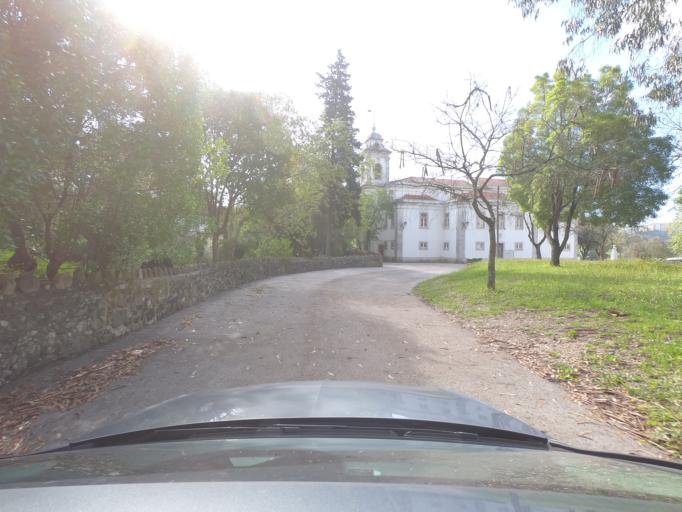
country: PT
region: Lisbon
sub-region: Oeiras
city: Carnaxide
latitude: 38.7221
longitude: -9.2500
